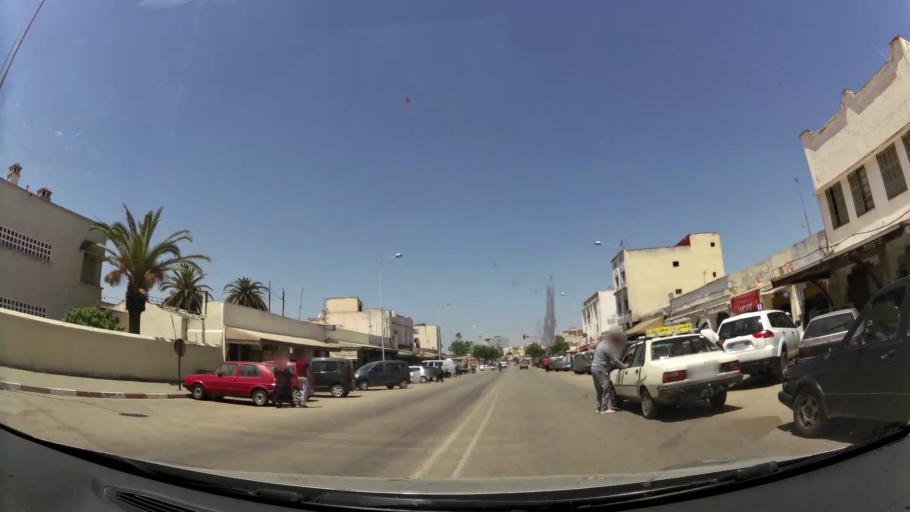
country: MA
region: Rabat-Sale-Zemmour-Zaer
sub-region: Khemisset
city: Khemisset
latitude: 33.8250
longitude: -6.0663
